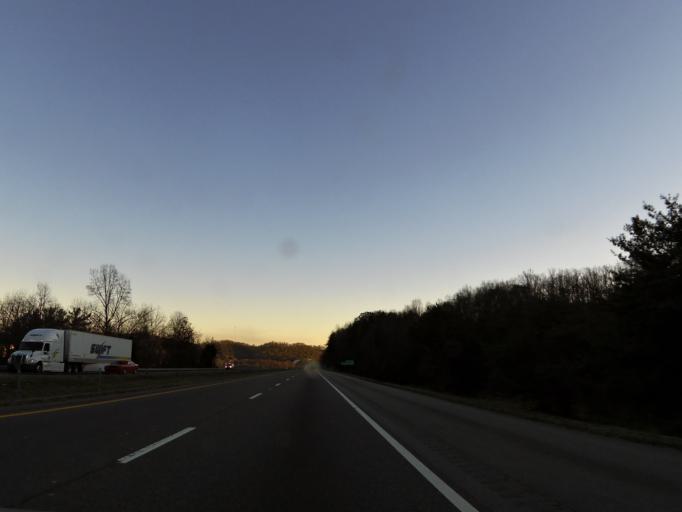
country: US
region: Tennessee
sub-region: Knox County
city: Knoxville
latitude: 36.0583
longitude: -84.0062
